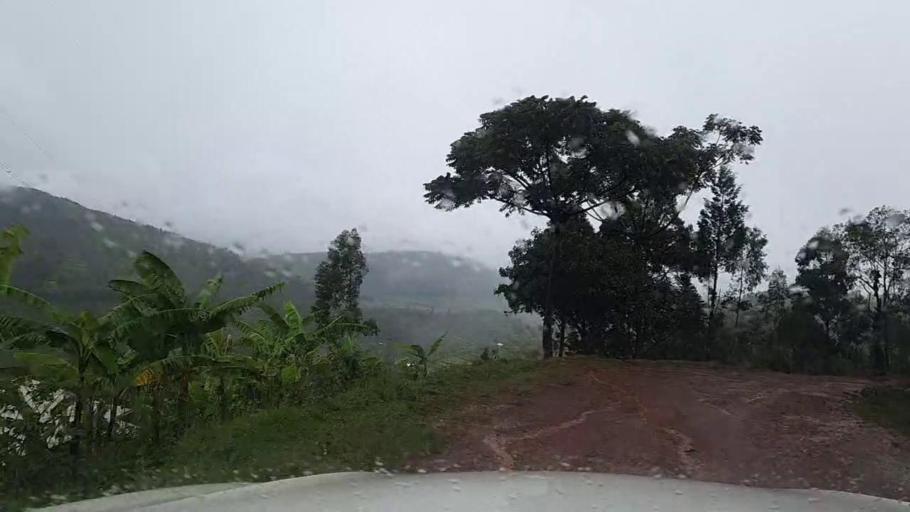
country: RW
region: Kigali
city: Kigali
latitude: -1.7644
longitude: 29.9918
